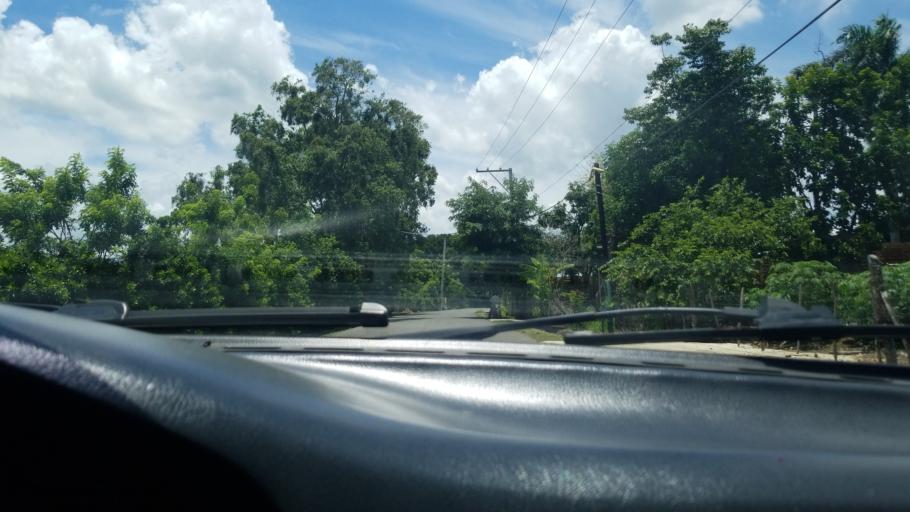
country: DO
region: Santiago
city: Santiago de los Caballeros
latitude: 19.4986
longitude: -70.6750
